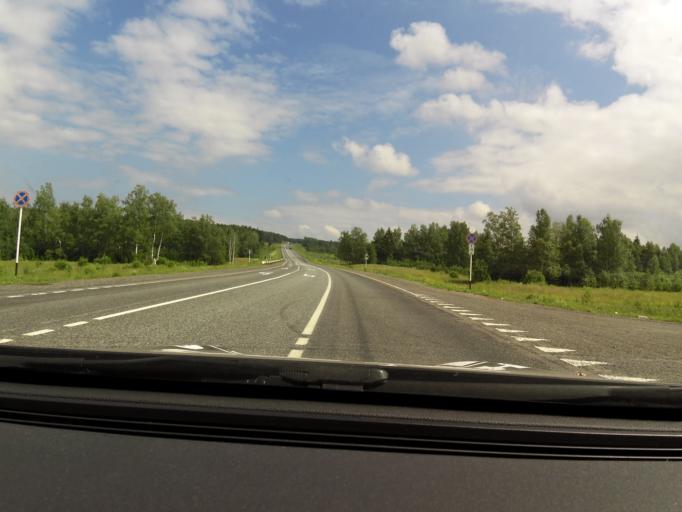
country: RU
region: Perm
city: Suksun
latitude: 57.0920
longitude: 57.3659
